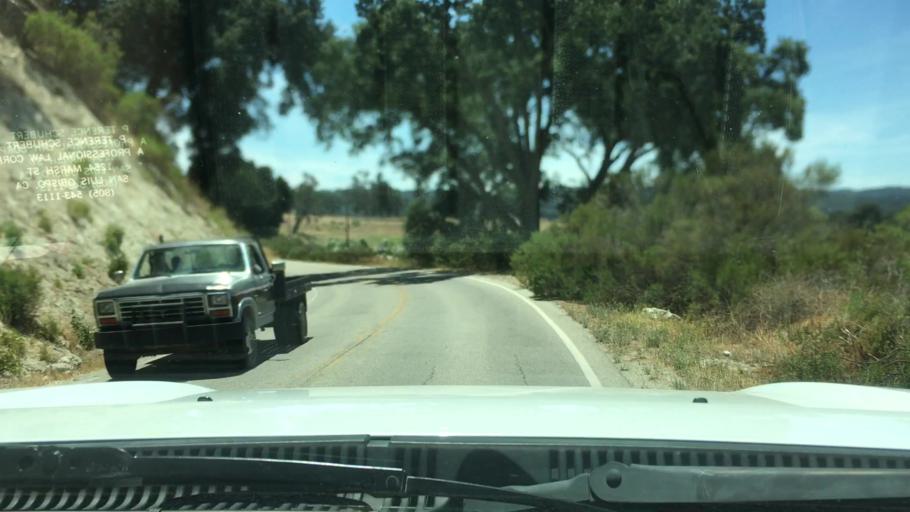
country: US
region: California
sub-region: San Luis Obispo County
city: Templeton
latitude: 35.5466
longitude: -120.6997
